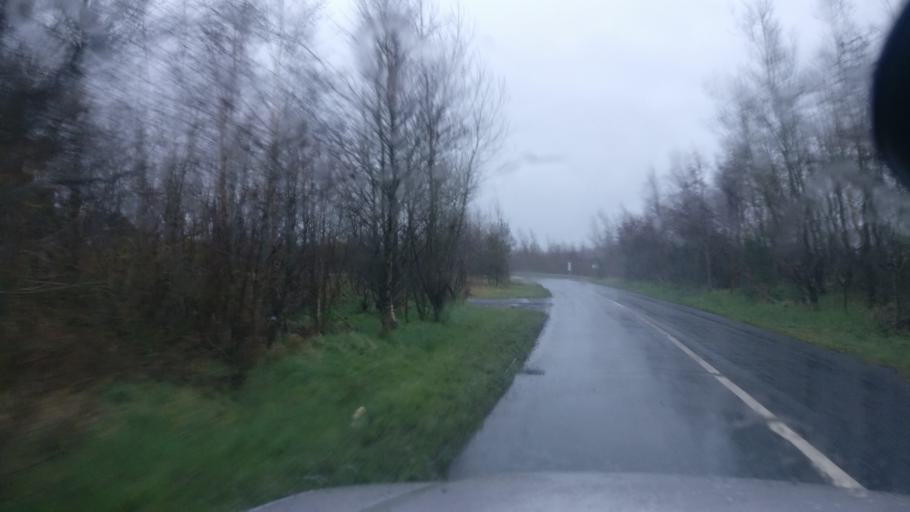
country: IE
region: Connaught
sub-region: County Galway
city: Ballinasloe
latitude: 53.3064
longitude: -8.3333
